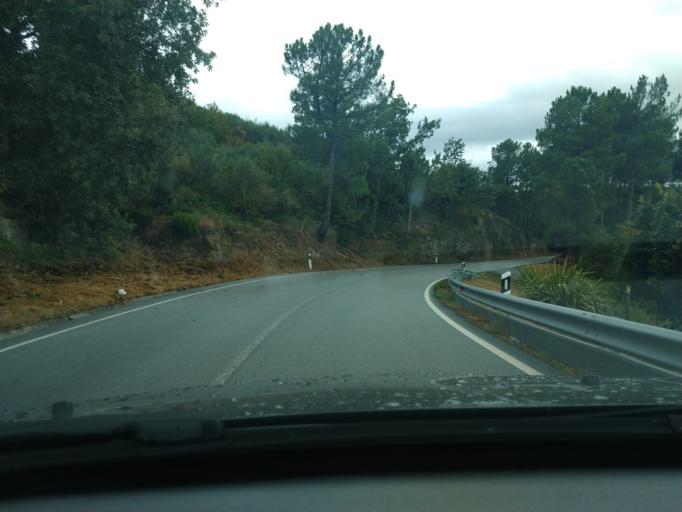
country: PT
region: Guarda
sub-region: Seia
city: Seia
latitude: 40.4132
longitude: -7.6956
